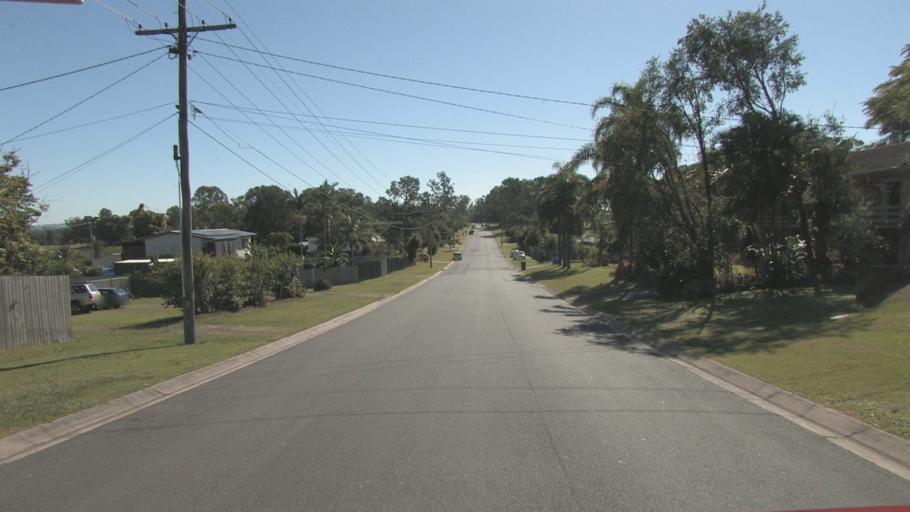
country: AU
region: Queensland
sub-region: Logan
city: Beenleigh
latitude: -27.7000
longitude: 153.2001
